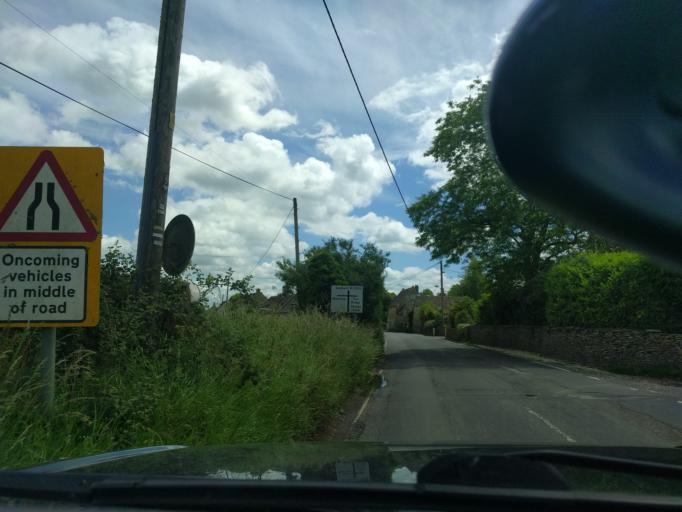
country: GB
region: England
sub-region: Wiltshire
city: Corsham
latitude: 51.4201
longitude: -2.1780
